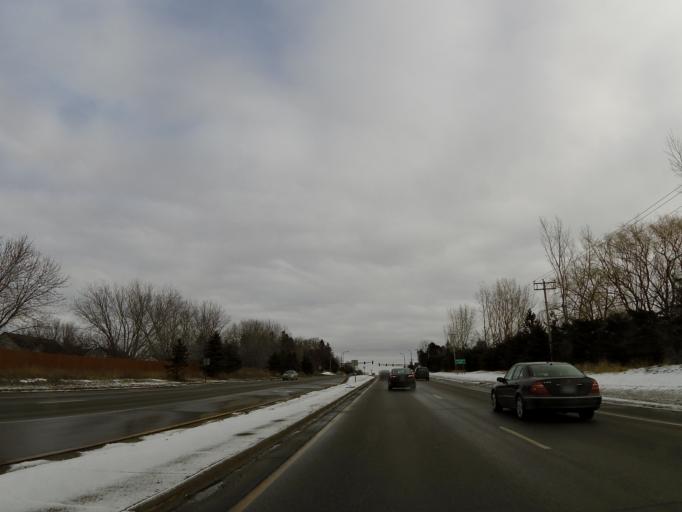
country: US
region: Minnesota
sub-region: Washington County
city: Woodbury
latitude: 44.9198
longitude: -92.9209
